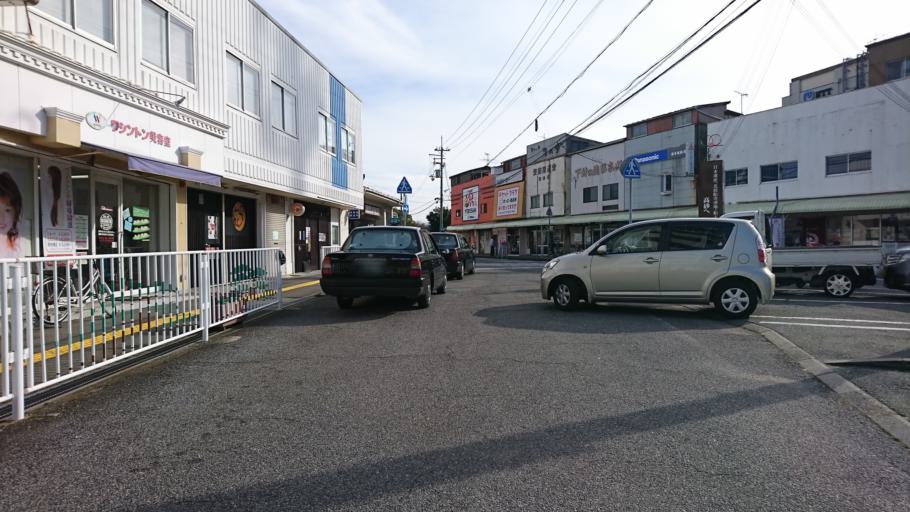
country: JP
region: Hyogo
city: Kakogawacho-honmachi
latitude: 34.7517
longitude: 134.8029
